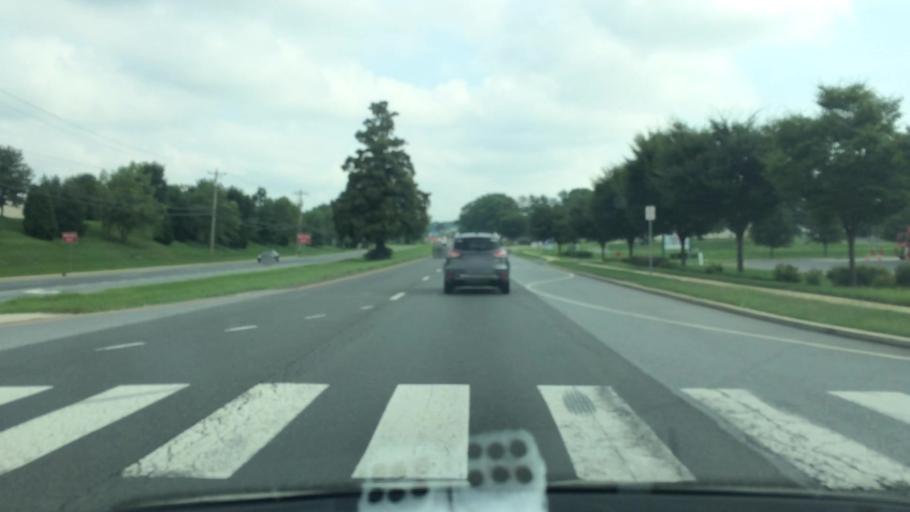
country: US
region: Delaware
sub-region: New Castle County
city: Bear
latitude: 39.6412
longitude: -75.6268
